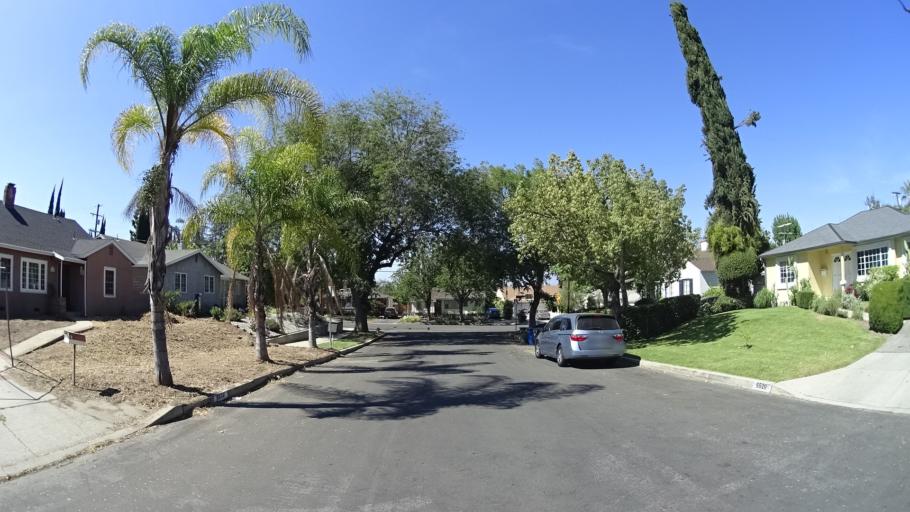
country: US
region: California
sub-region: Los Angeles County
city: Van Nuys
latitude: 34.1708
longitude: -118.4172
